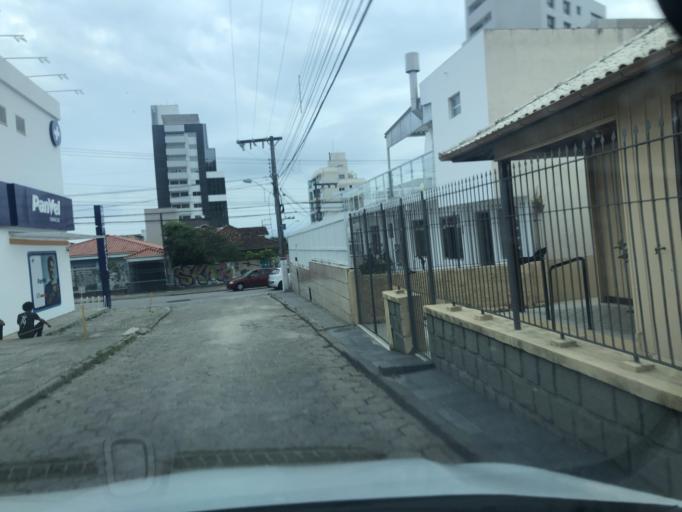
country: BR
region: Santa Catarina
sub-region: Florianopolis
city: Saco dos Limoes
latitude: -27.6074
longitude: -48.5341
